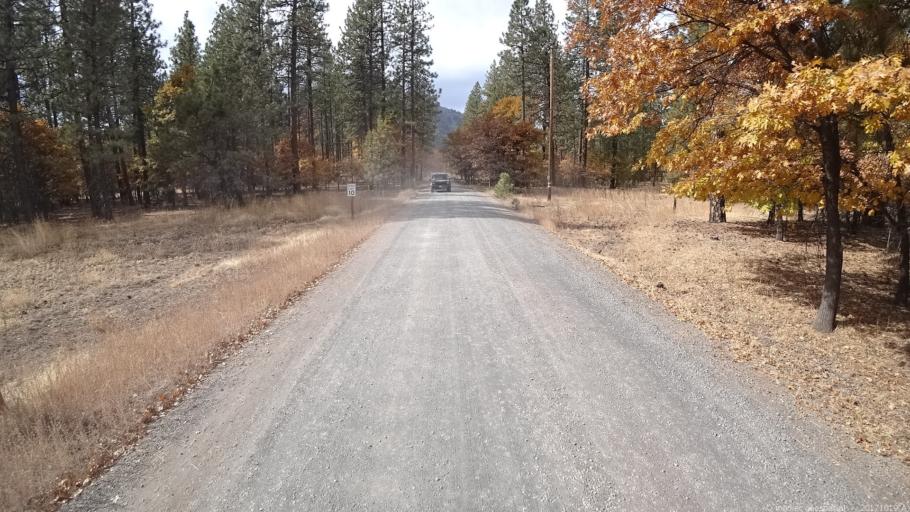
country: US
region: California
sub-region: Shasta County
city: Burney
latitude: 41.0799
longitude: -121.5308
